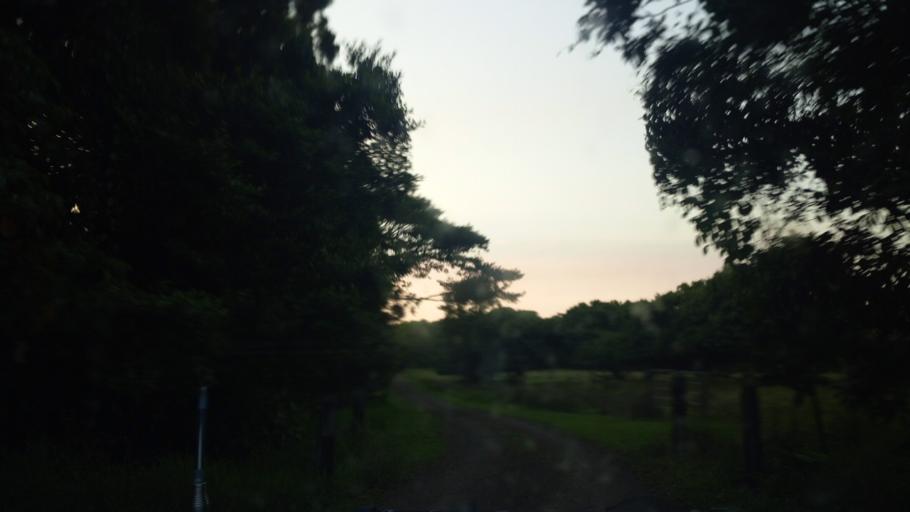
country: AU
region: Queensland
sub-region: Tablelands
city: Atherton
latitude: -17.3673
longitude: 145.7524
